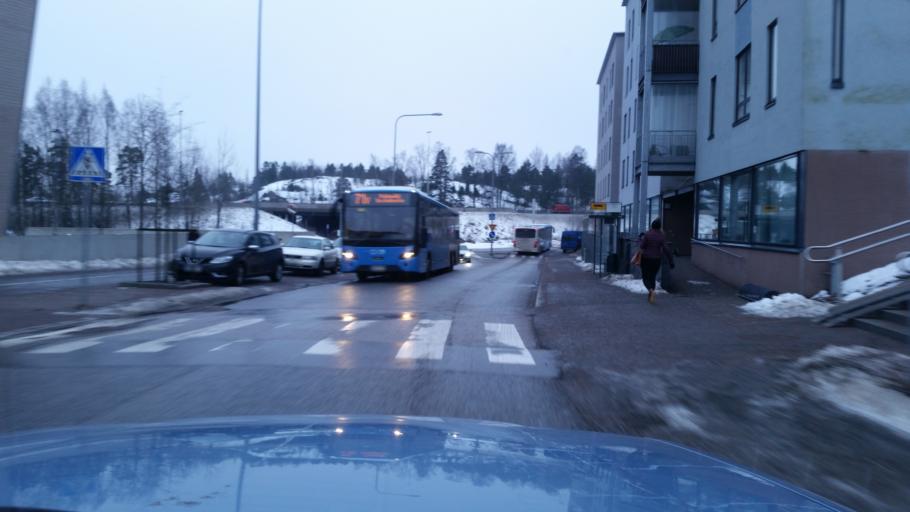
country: FI
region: Uusimaa
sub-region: Helsinki
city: Helsinki
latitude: 60.2245
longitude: 24.9886
